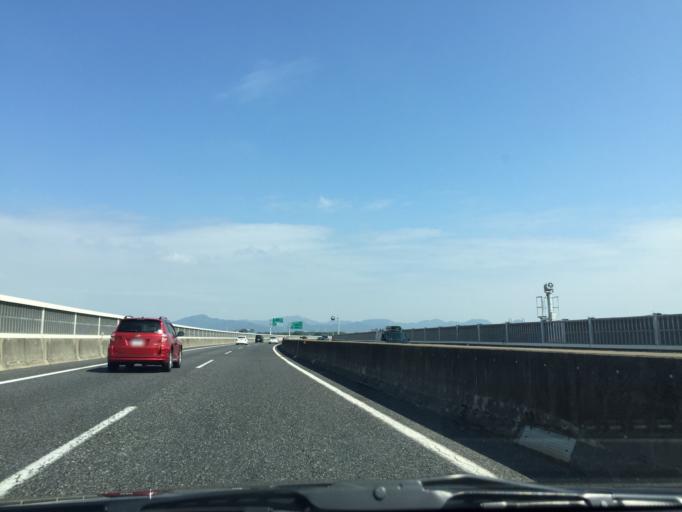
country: JP
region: Aichi
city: Kuroda
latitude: 35.3493
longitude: 136.7938
